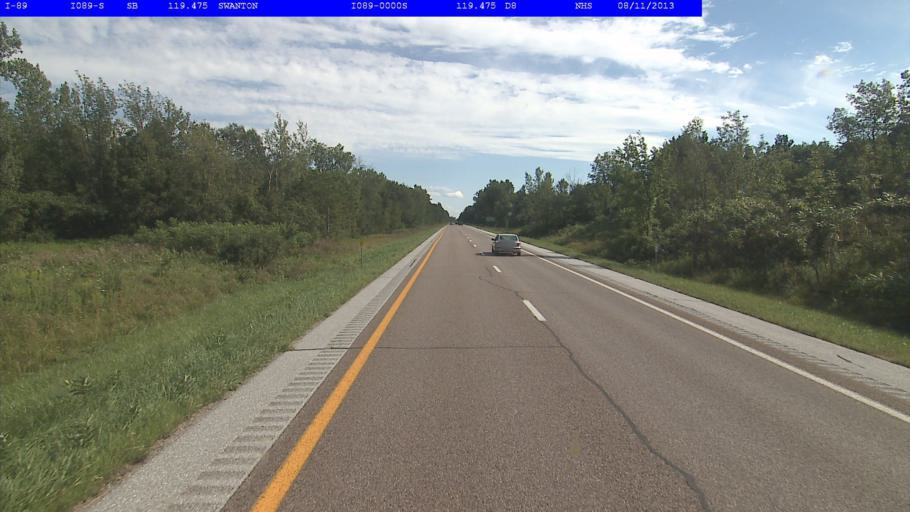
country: US
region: Vermont
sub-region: Franklin County
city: Saint Albans
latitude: 44.8694
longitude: -73.0829
